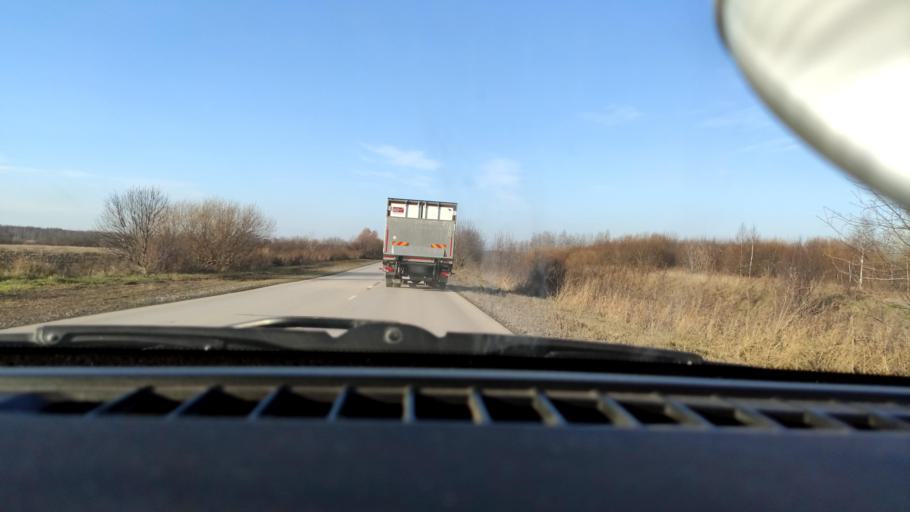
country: RU
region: Perm
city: Kondratovo
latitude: 57.9990
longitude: 56.0764
